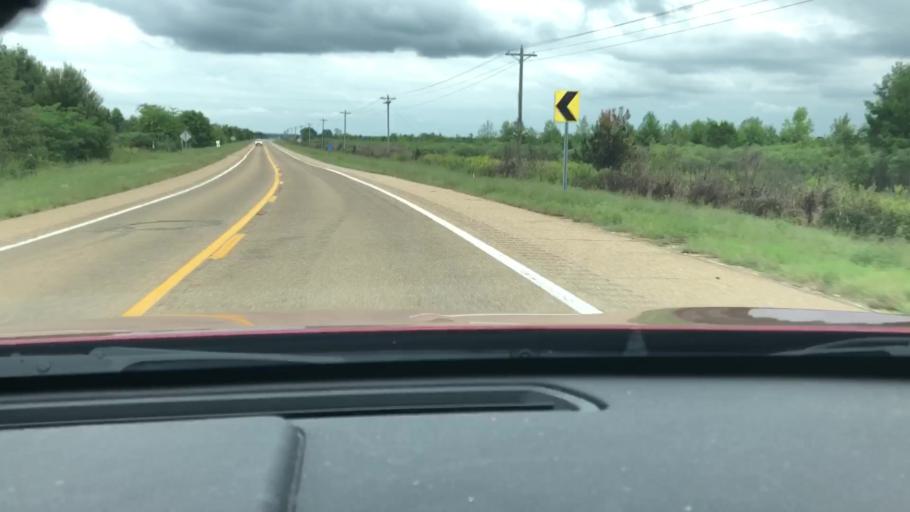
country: US
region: Arkansas
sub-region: Miller County
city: Texarkana
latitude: 33.4127
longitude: -93.8060
